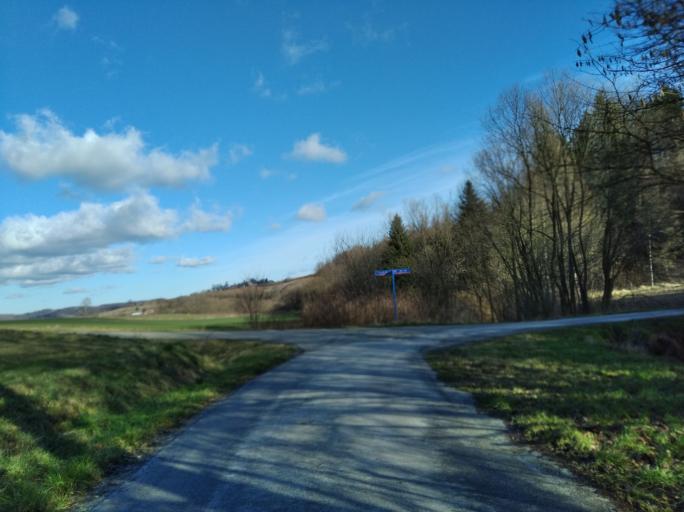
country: PL
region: Subcarpathian Voivodeship
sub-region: Powiat strzyzowski
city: Wisniowa
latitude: 49.9024
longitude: 21.6862
